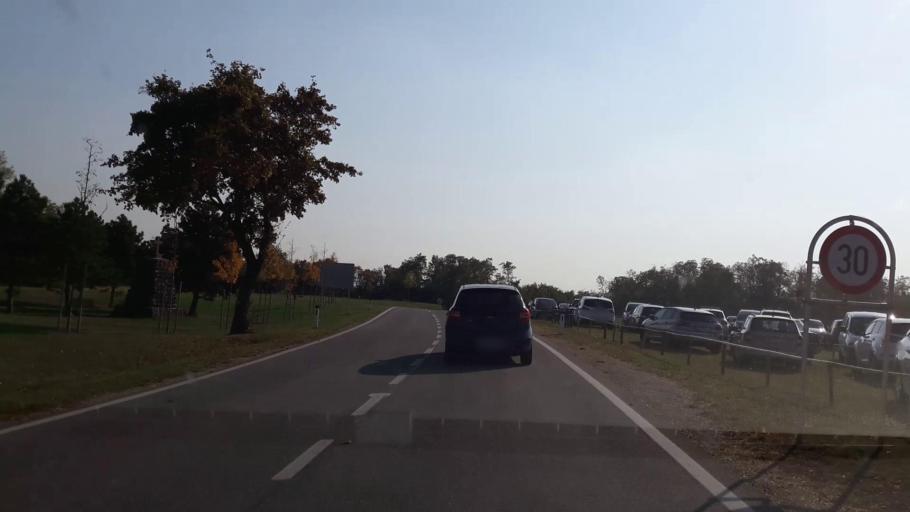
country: AT
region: Lower Austria
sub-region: Politischer Bezirk Ganserndorf
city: Marchegg
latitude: 48.2157
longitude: 16.9298
